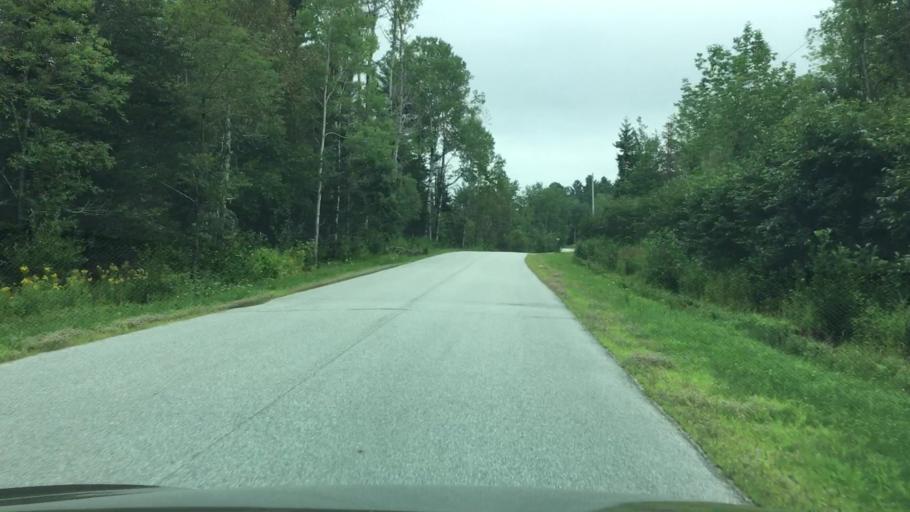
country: US
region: Maine
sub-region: Waldo County
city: Stockton Springs
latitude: 44.5281
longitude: -68.8289
